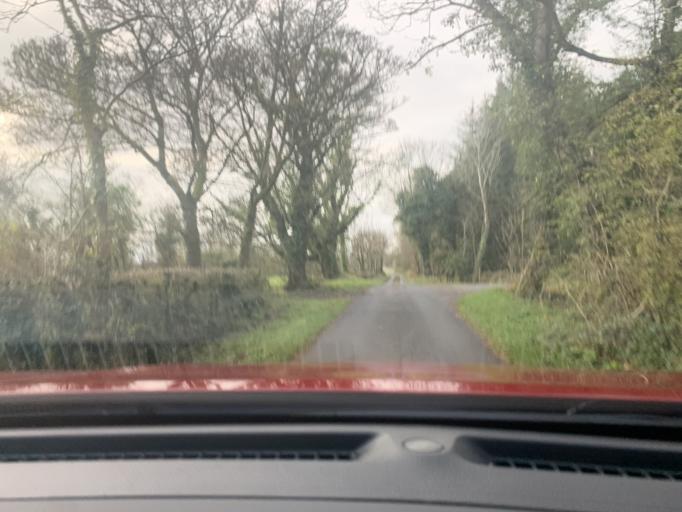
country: IE
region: Connaught
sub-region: Roscommon
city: Ballaghaderreen
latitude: 54.0150
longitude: -8.6170
